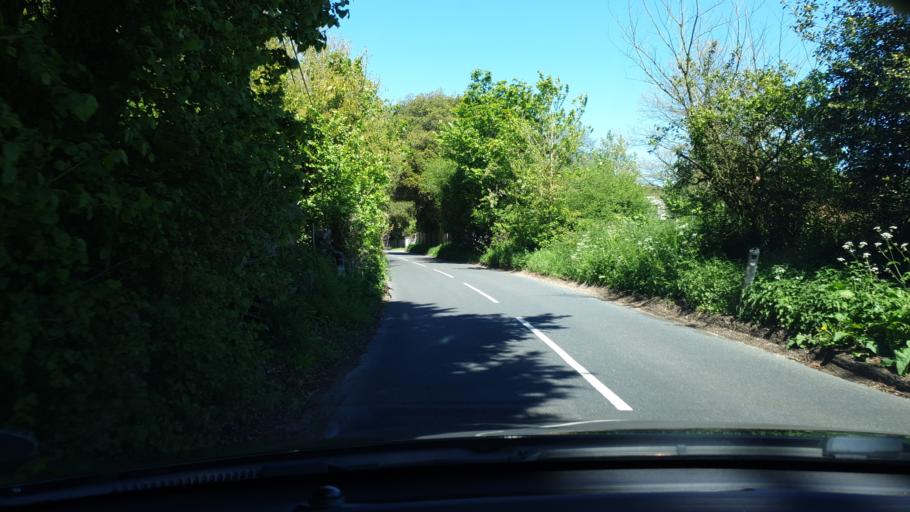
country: GB
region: England
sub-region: Essex
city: Little Clacton
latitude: 51.8687
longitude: 1.1250
